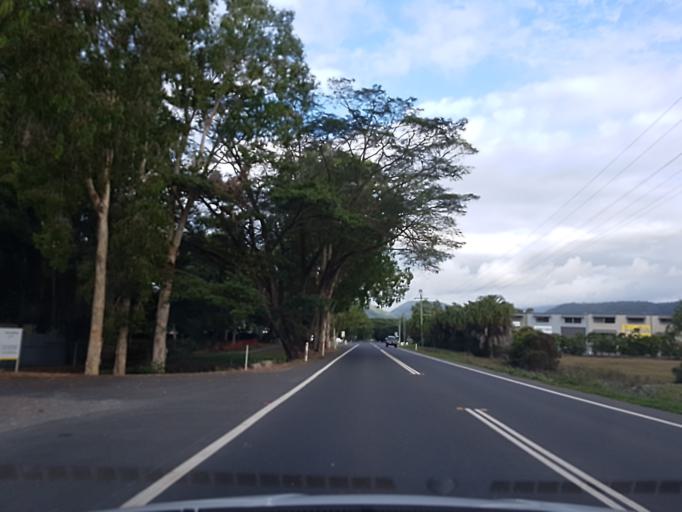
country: AU
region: Queensland
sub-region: Cairns
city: Port Douglas
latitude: -16.5369
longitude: 145.4686
